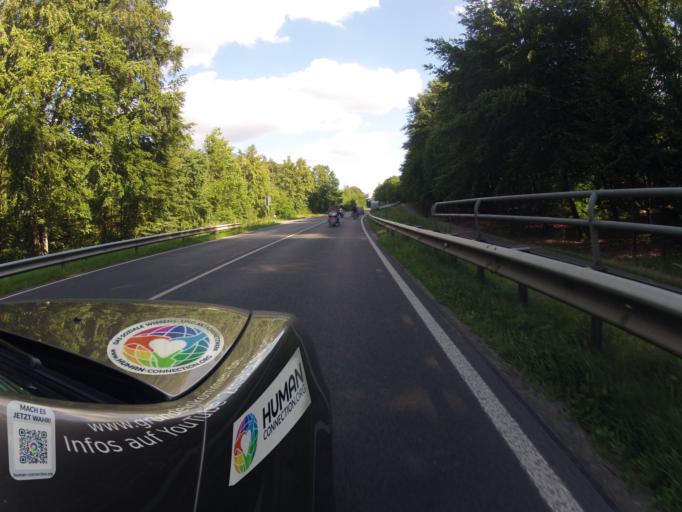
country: DE
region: Mecklenburg-Vorpommern
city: Seebad Bansin
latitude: 53.9716
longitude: 14.1174
